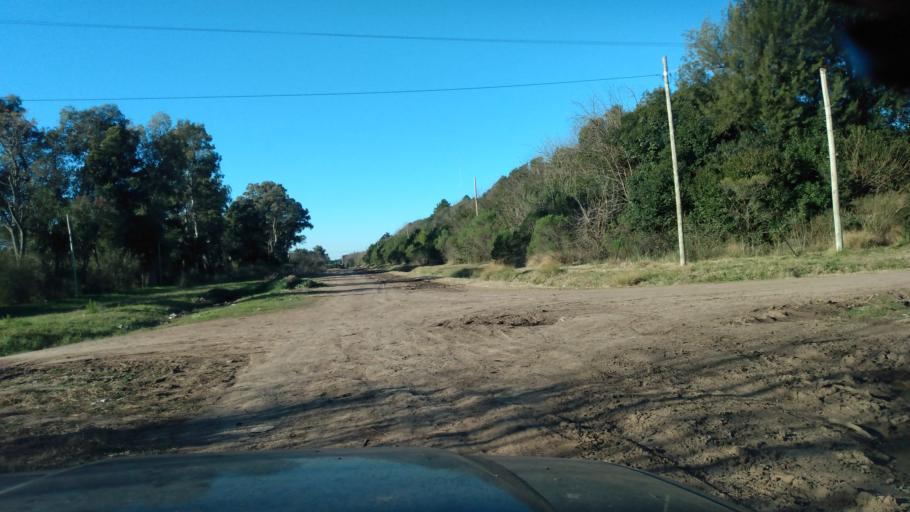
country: AR
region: Buenos Aires
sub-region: Partido de Lujan
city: Lujan
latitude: -34.5546
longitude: -59.1494
